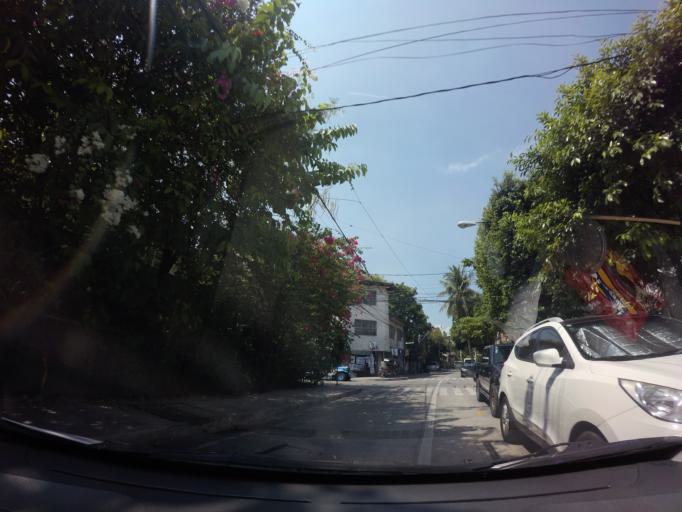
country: PH
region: Metro Manila
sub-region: Makati City
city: Makati City
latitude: 14.5653
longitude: 121.0063
